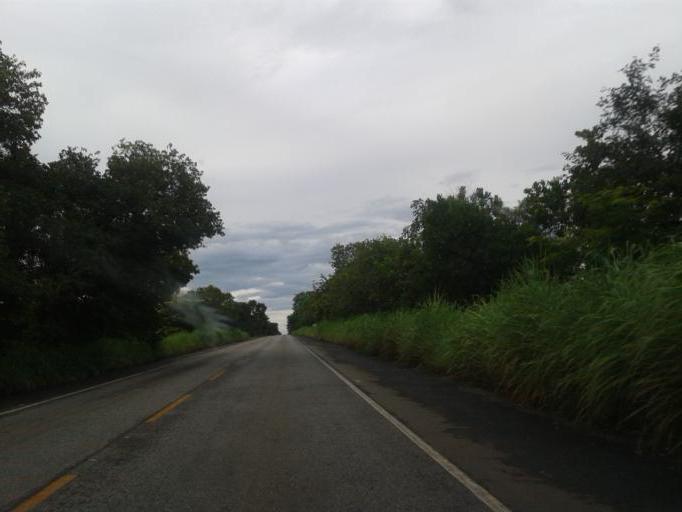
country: BR
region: Goias
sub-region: Mozarlandia
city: Mozarlandia
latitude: -14.8171
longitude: -50.5313
